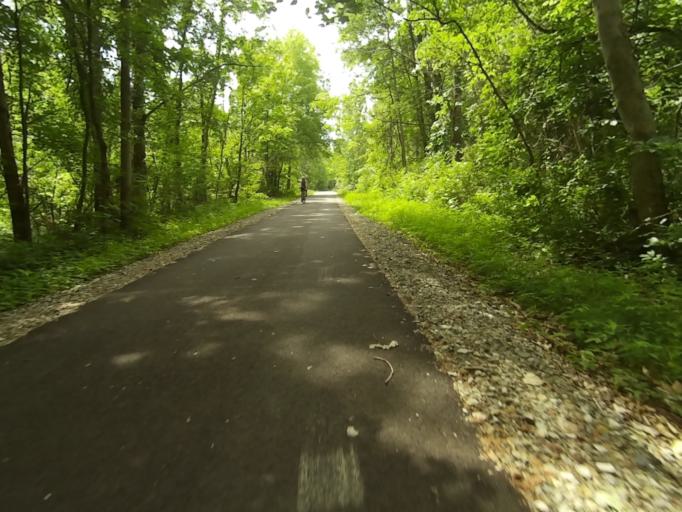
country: US
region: Ohio
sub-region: Summit County
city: Boston Heights
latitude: 41.2515
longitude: -81.5163
